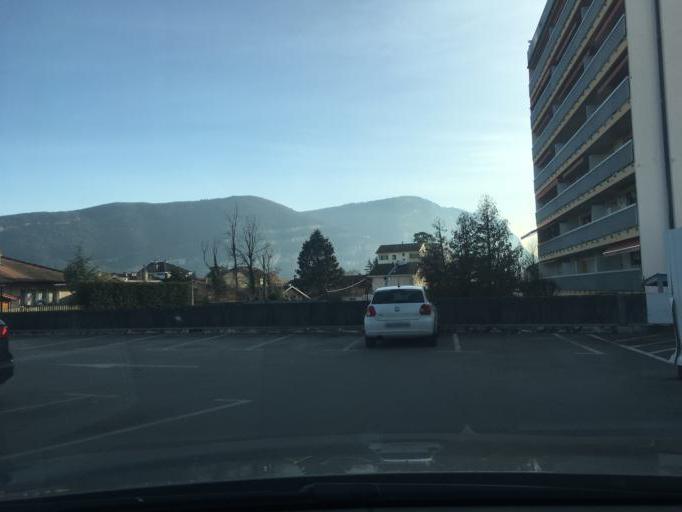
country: FR
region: Rhone-Alpes
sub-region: Departement de la Haute-Savoie
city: Gaillard
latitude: 46.1909
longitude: 6.2155
